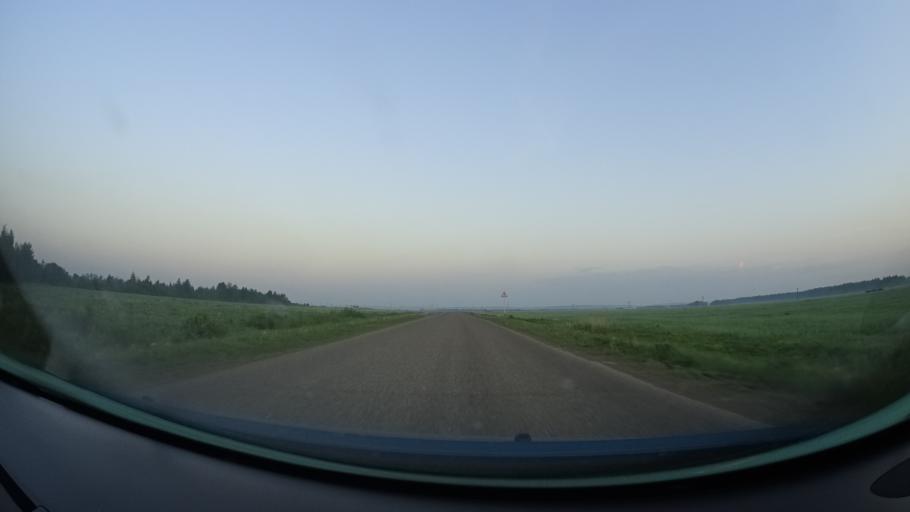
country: RU
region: Bashkortostan
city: Starobaltachevo
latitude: 56.0376
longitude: 55.9356
